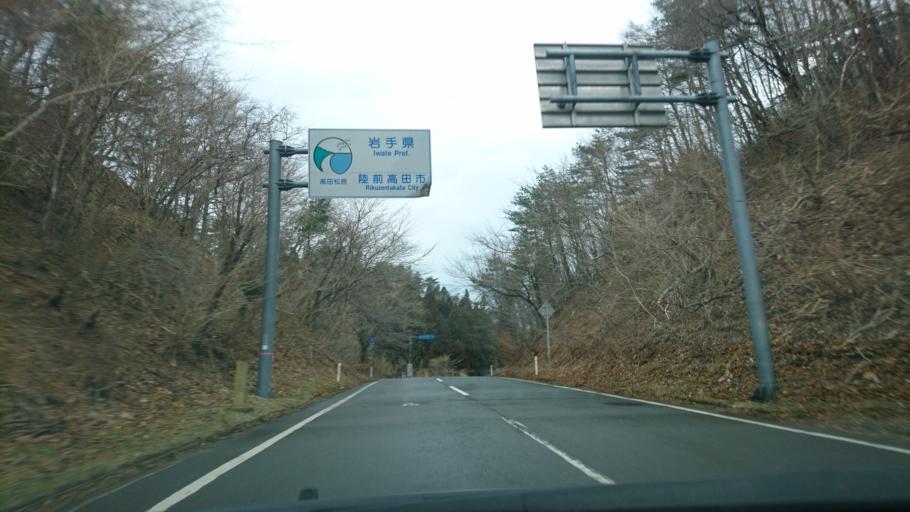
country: JP
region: Iwate
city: Ofunato
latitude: 38.9959
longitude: 141.5470
